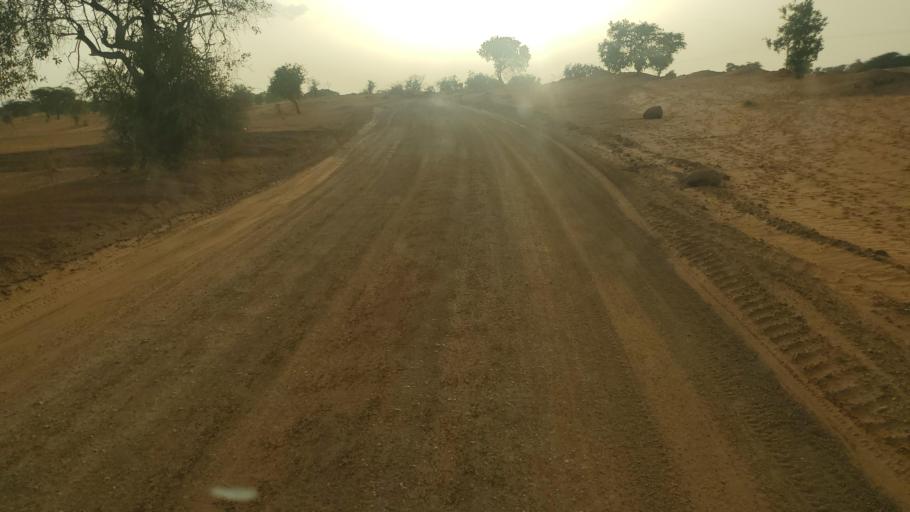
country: SN
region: Louga
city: Dara
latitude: 15.3621
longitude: -15.5471
